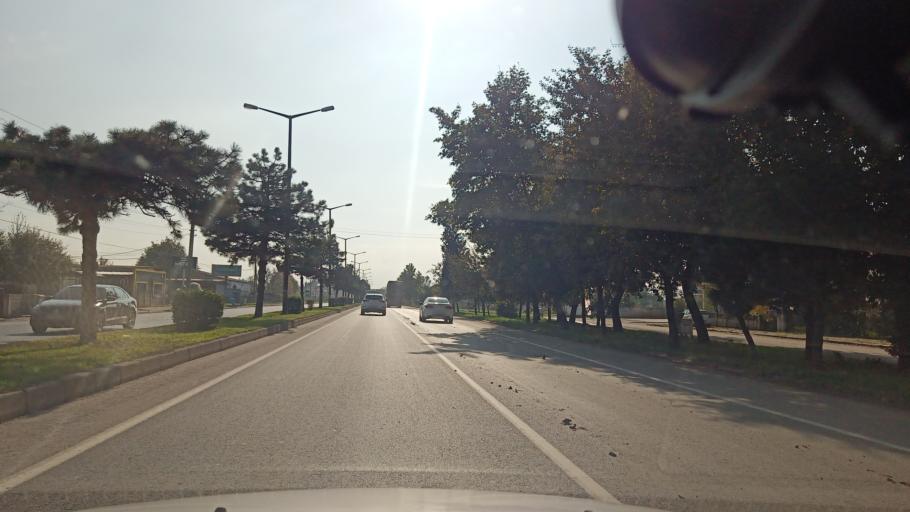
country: TR
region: Sakarya
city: Adapazari
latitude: 40.8075
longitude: 30.4055
